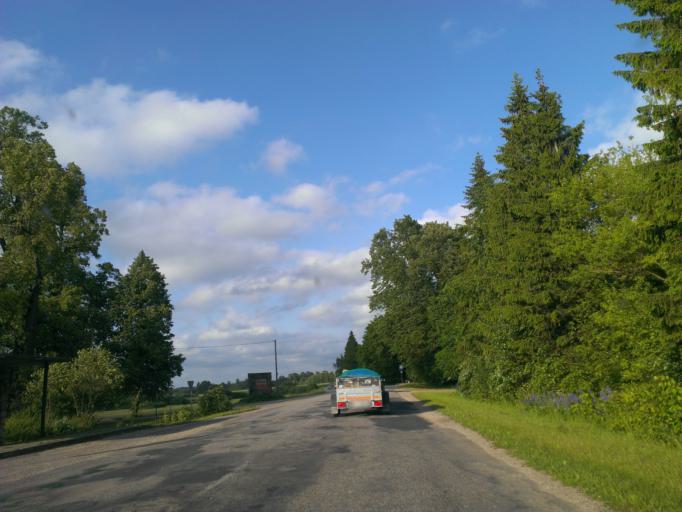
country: LV
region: Aizpute
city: Aizpute
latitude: 56.7309
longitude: 21.6629
